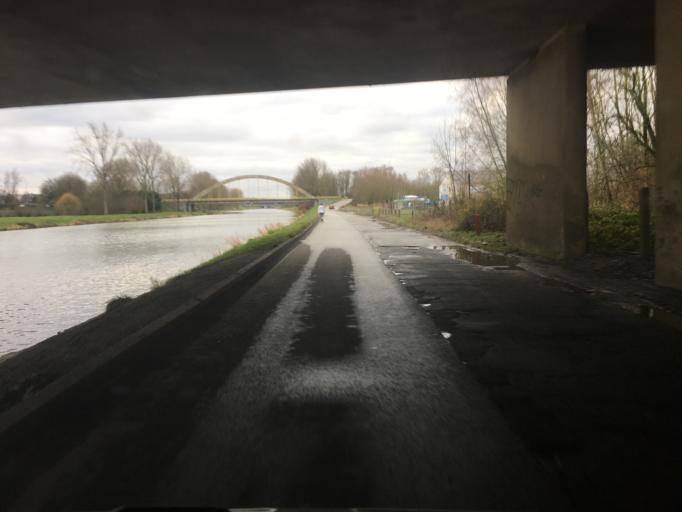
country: BE
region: Wallonia
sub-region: Province du Hainaut
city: Manage
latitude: 50.5112
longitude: 4.2116
